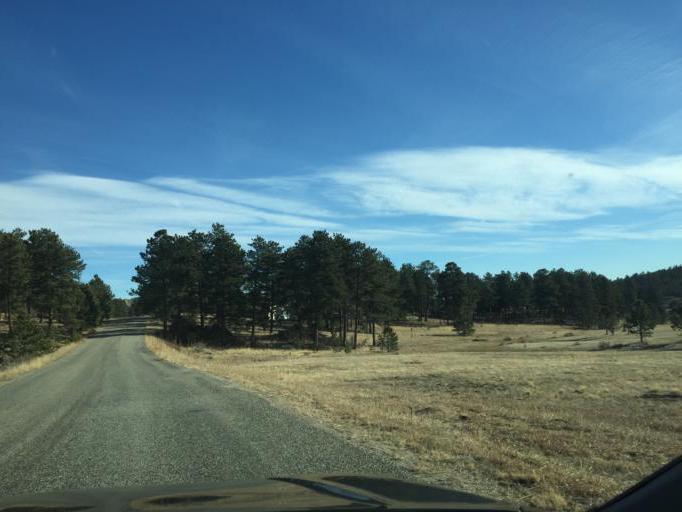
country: US
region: Colorado
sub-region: Jefferson County
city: Evergreen
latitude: 39.4424
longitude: -105.4571
